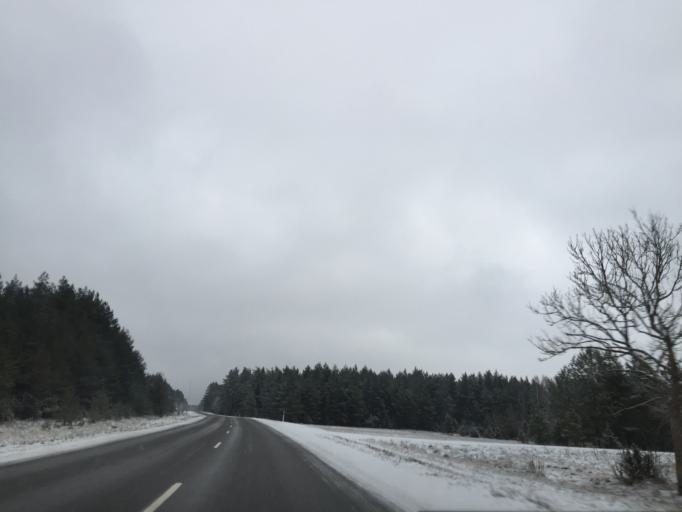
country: EE
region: Laeaene
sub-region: Lihula vald
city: Lihula
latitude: 58.6108
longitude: 23.9298
